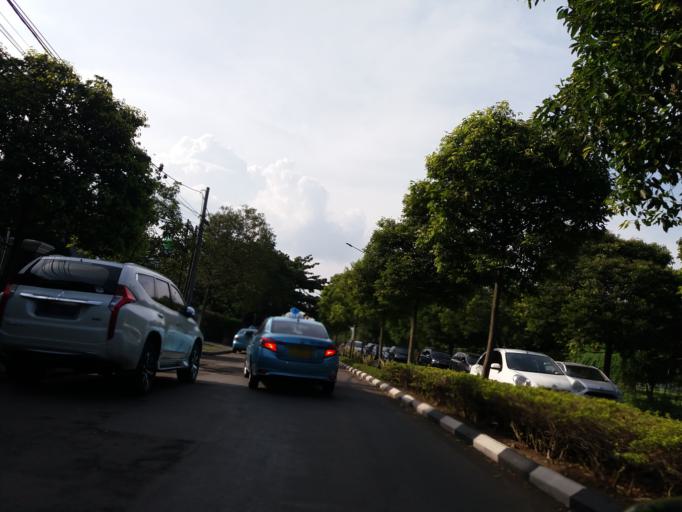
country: ID
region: West Java
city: Bandung
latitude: -6.9596
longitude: 107.6262
